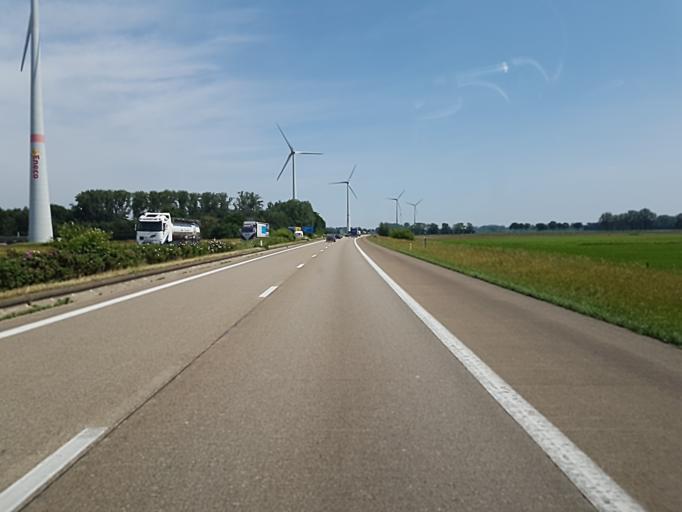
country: BE
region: Flanders
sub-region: Provincie Antwerpen
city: Arendonk
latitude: 51.2973
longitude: 5.0574
